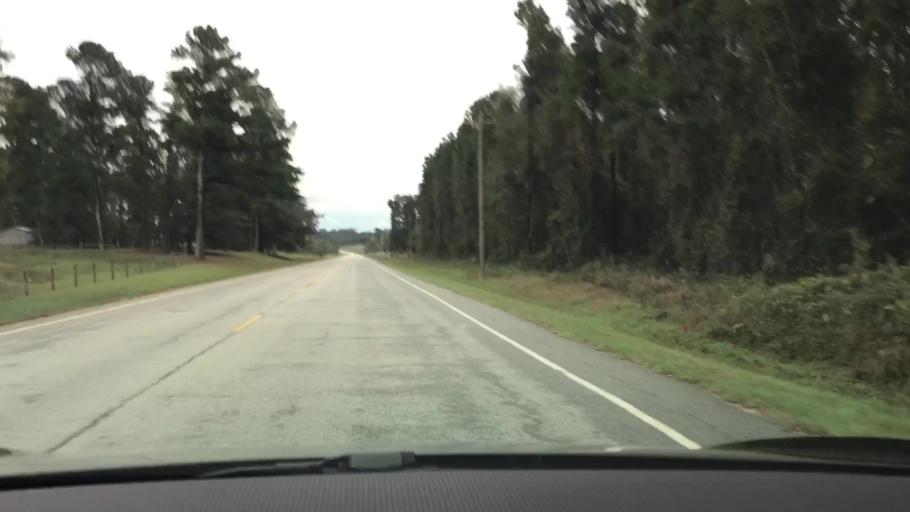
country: US
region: Georgia
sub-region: Jefferson County
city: Wrens
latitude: 33.1379
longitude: -82.4553
